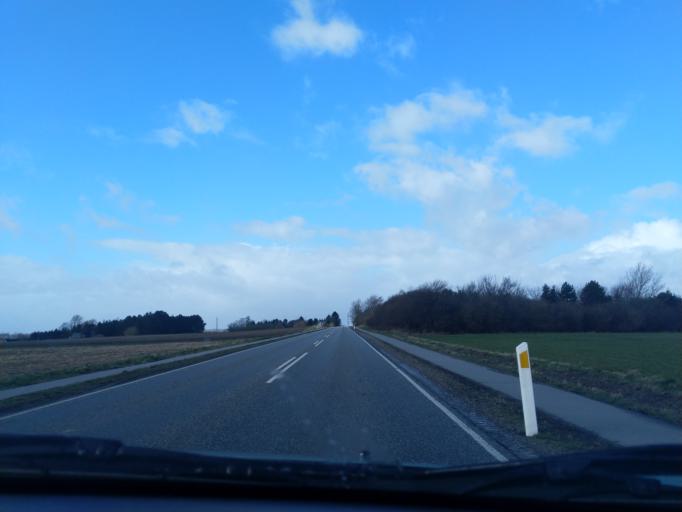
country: DK
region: Zealand
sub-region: Naestved Kommune
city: Naestved
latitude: 55.2748
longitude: 11.7290
